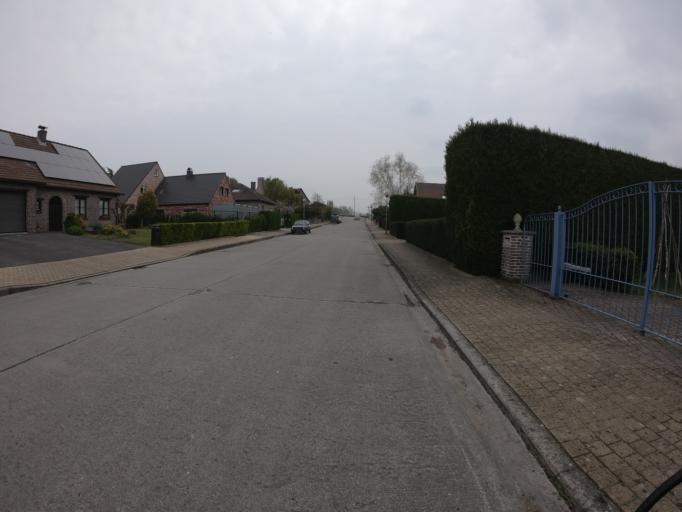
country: BE
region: Flanders
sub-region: Provincie Oost-Vlaanderen
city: Ronse
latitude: 50.7451
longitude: 3.6228
